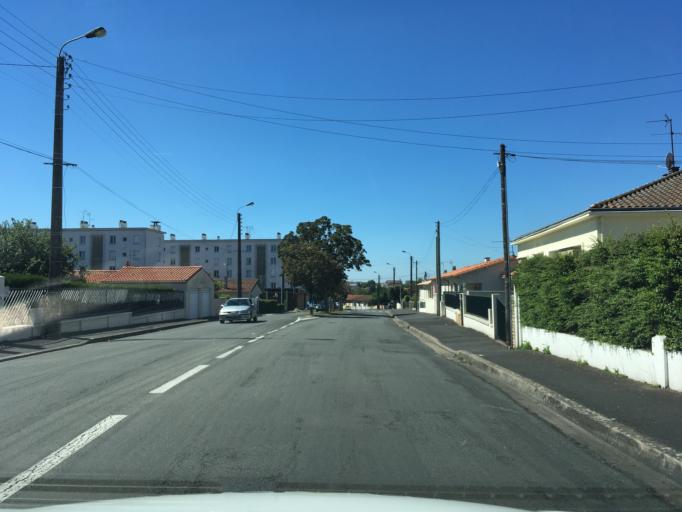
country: FR
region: Poitou-Charentes
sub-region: Departement des Deux-Sevres
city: Niort
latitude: 46.3255
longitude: -0.4386
